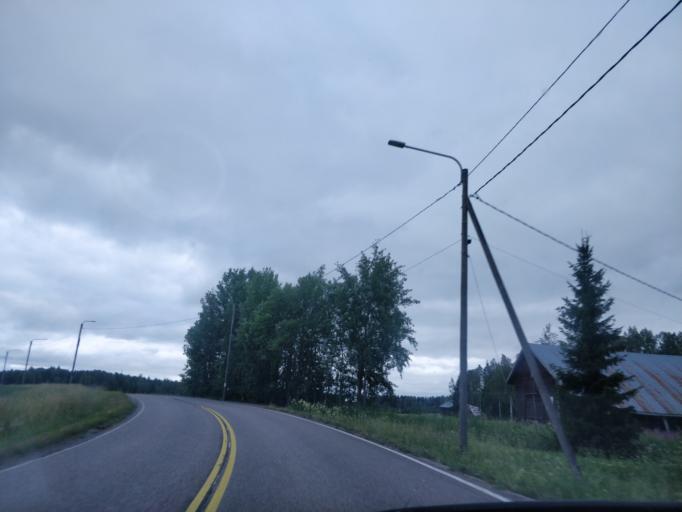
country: FI
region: Uusimaa
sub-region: Helsinki
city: Kauniainen
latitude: 60.2904
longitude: 24.6990
